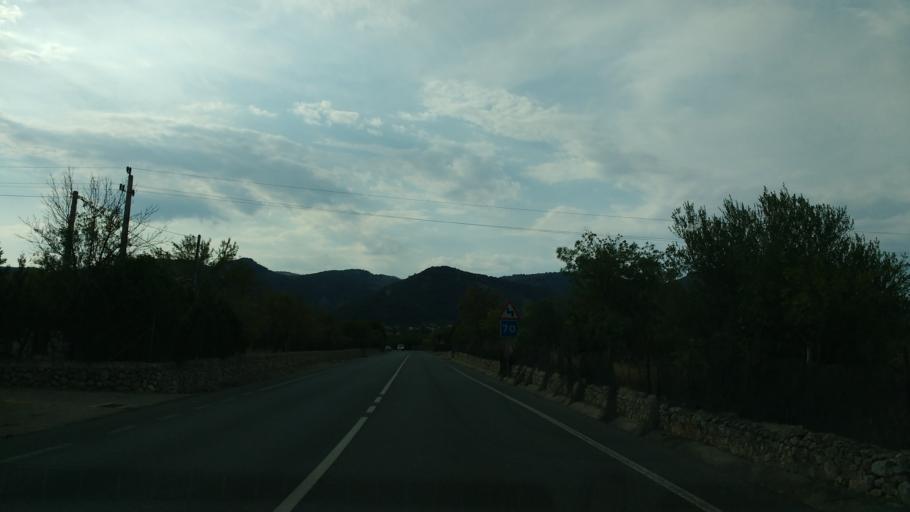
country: ES
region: Balearic Islands
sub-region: Illes Balears
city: Alaro
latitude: 39.6952
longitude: 2.8033
